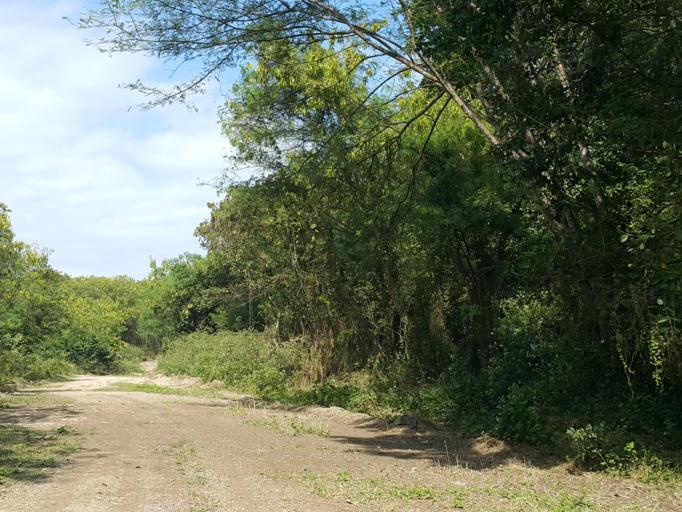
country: TH
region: Lampang
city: Mae Mo
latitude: 18.3331
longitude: 99.7673
